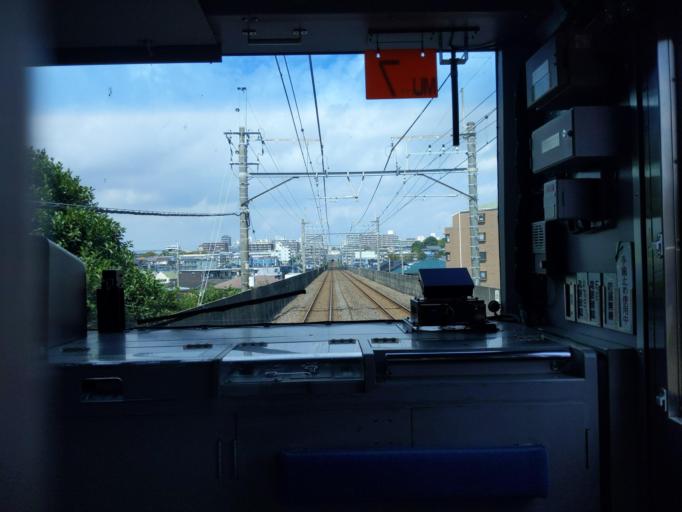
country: JP
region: Chiba
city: Matsudo
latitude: 35.7832
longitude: 139.9406
